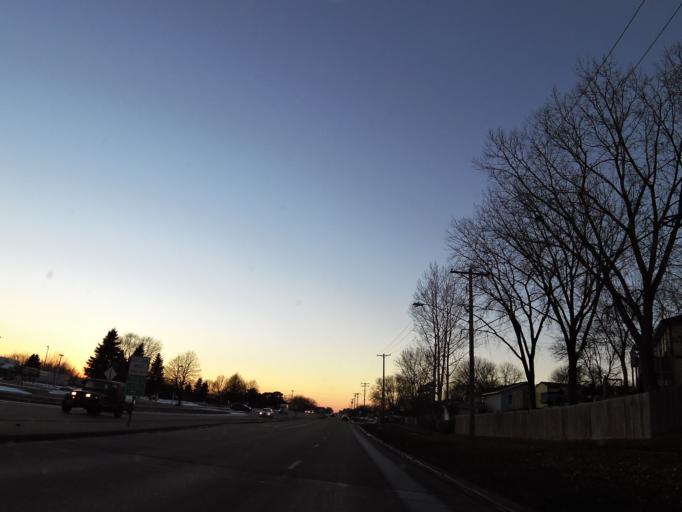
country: US
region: Minnesota
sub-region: Scott County
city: Savage
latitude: 44.8080
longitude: -93.3594
